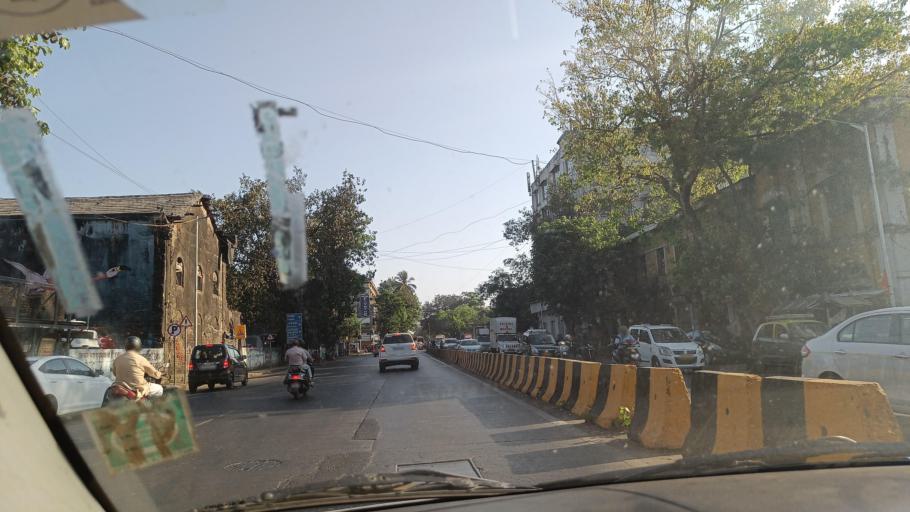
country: IN
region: Maharashtra
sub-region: Raigarh
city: Uran
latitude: 18.9502
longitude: 72.8409
